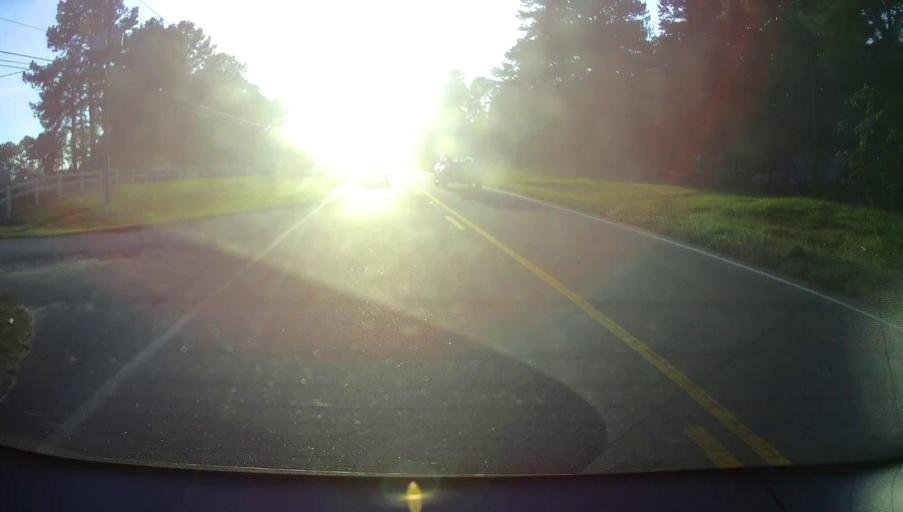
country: US
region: Georgia
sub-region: Houston County
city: Centerville
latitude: 32.6736
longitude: -83.7139
